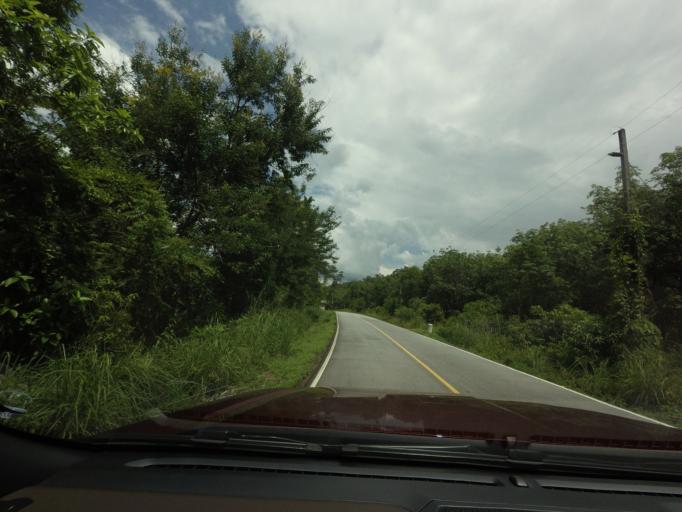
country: TH
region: Narathiwat
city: Chanae
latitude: 6.0512
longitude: 101.6879
